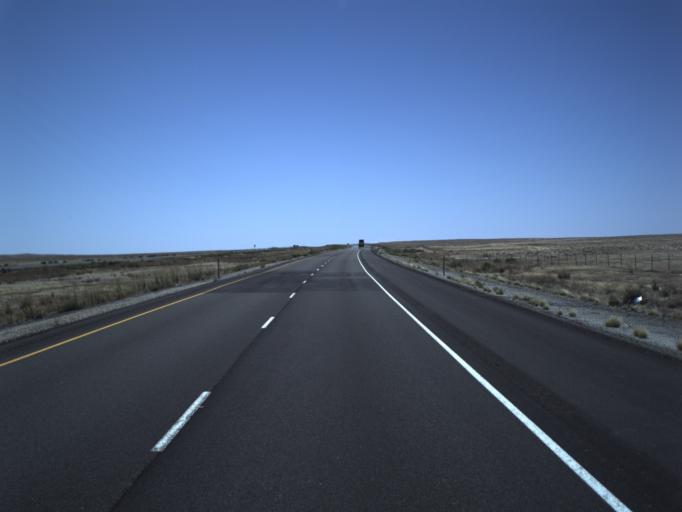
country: US
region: Colorado
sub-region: Mesa County
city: Loma
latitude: 39.0698
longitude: -109.2411
